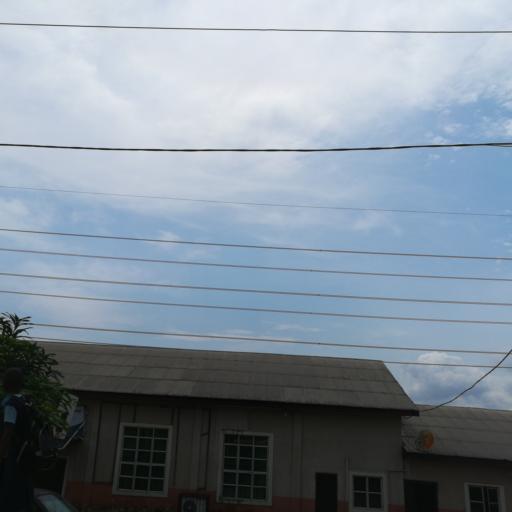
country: NG
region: Rivers
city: Port Harcourt
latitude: 4.8690
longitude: 7.0156
